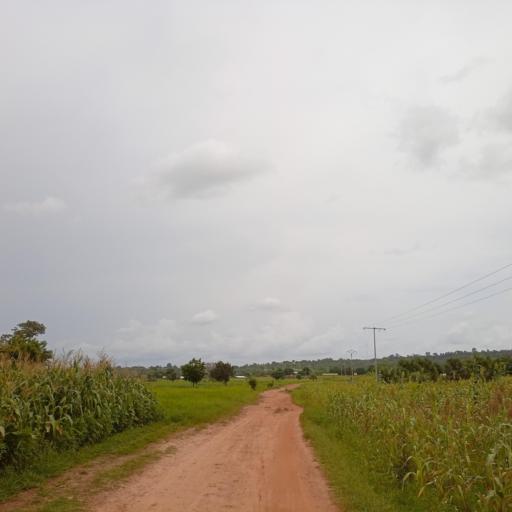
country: TG
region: Savanes
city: Dapaong
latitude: 10.8070
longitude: 0.0281
